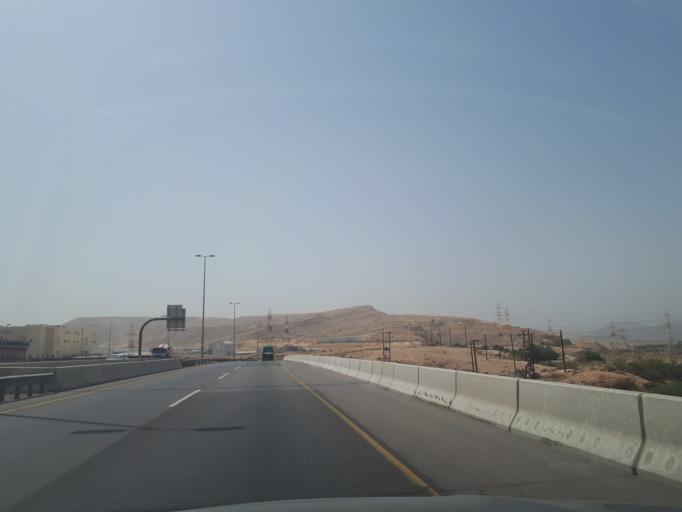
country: OM
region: Muhafazat Masqat
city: As Sib al Jadidah
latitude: 23.5570
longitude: 58.1930
